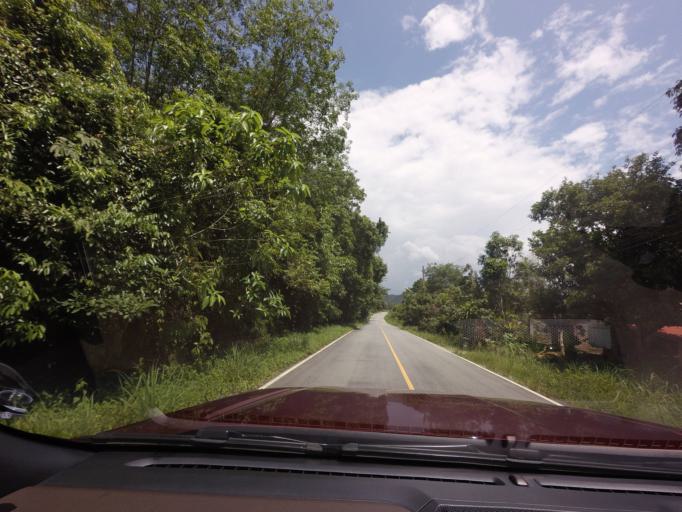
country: TH
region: Narathiwat
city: Chanae
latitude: 6.0792
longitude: 101.6886
